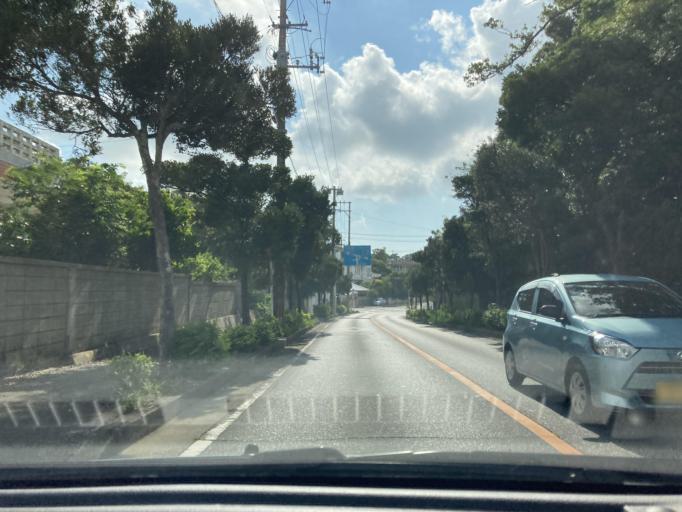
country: JP
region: Okinawa
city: Tomigusuku
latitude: 26.1431
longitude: 127.7673
